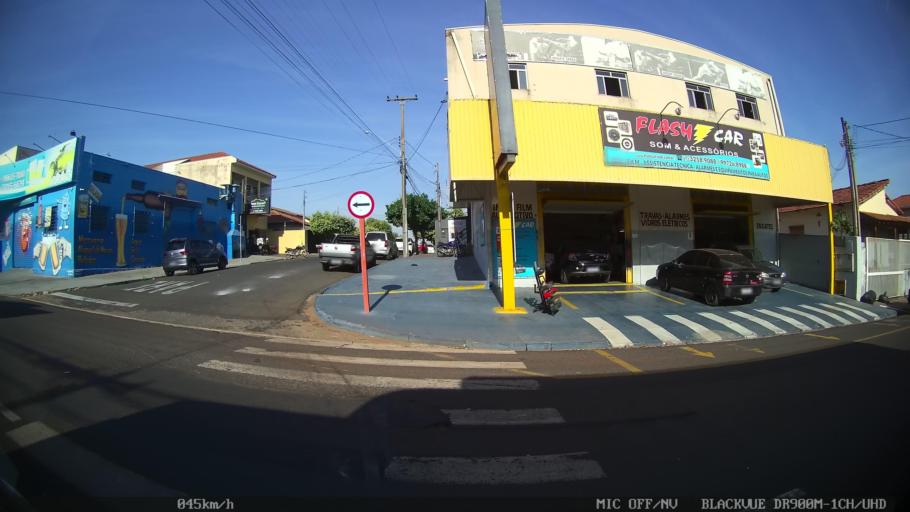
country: BR
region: Sao Paulo
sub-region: Sao Jose Do Rio Preto
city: Sao Jose do Rio Preto
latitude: -20.7964
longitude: -49.3649
